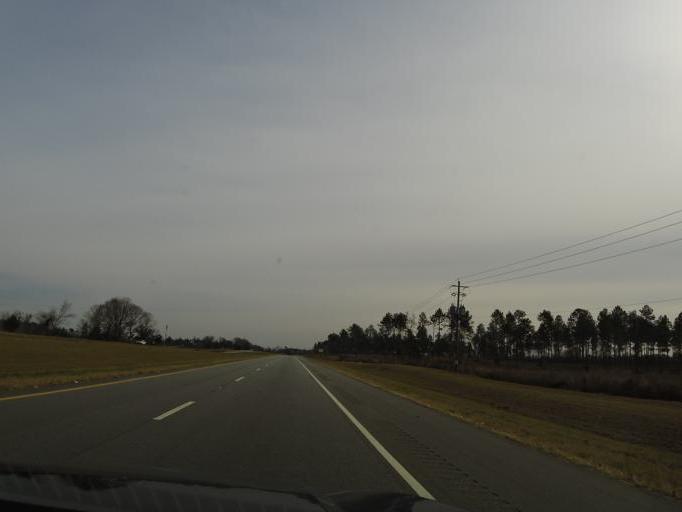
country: US
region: Georgia
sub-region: Seminole County
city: Donalsonville
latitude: 31.1070
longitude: -85.0215
